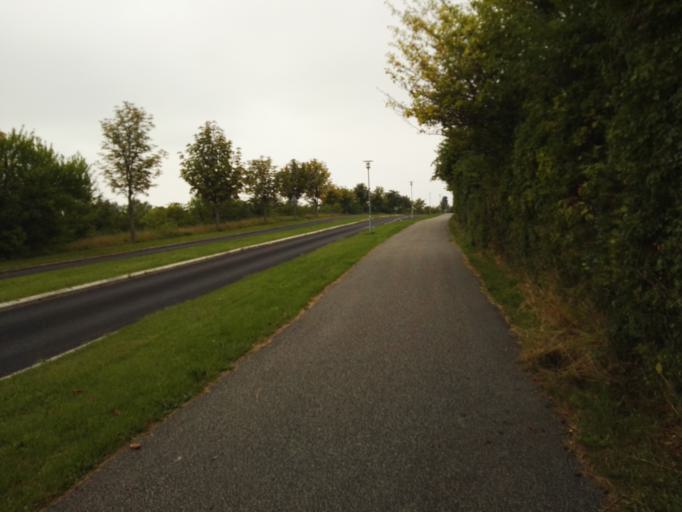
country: DK
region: Capital Region
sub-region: Egedal Kommune
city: Vekso
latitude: 55.7509
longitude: 12.2367
